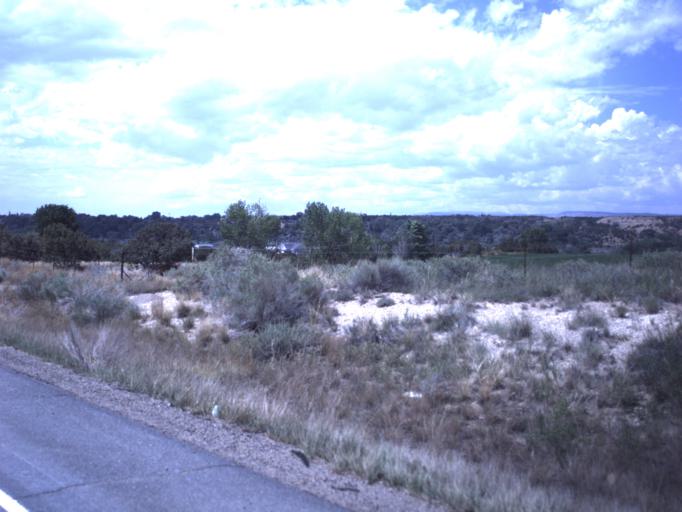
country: US
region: Utah
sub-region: Duchesne County
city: Duchesne
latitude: 40.1671
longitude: -110.3618
